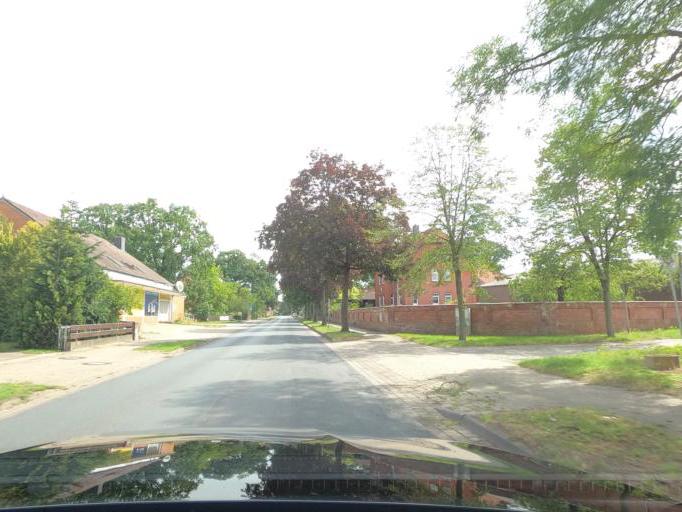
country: DE
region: Lower Saxony
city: Isernhagen Farster Bauerschaft
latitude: 52.5104
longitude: 9.8764
